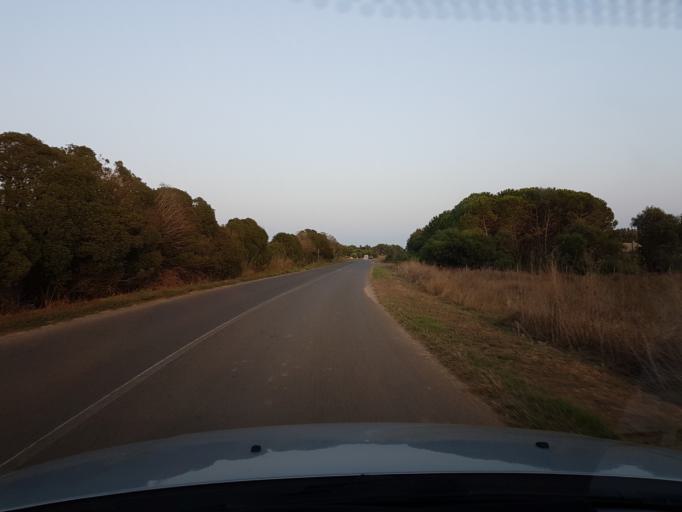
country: IT
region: Sardinia
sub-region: Provincia di Oristano
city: Cabras
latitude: 39.9502
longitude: 8.4265
